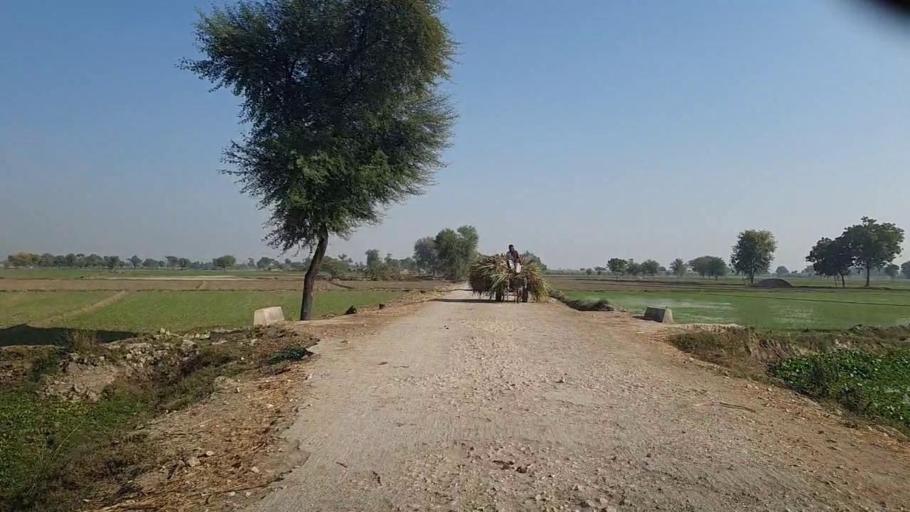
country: PK
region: Sindh
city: Darya Khan Marri
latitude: 26.6553
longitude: 68.3543
